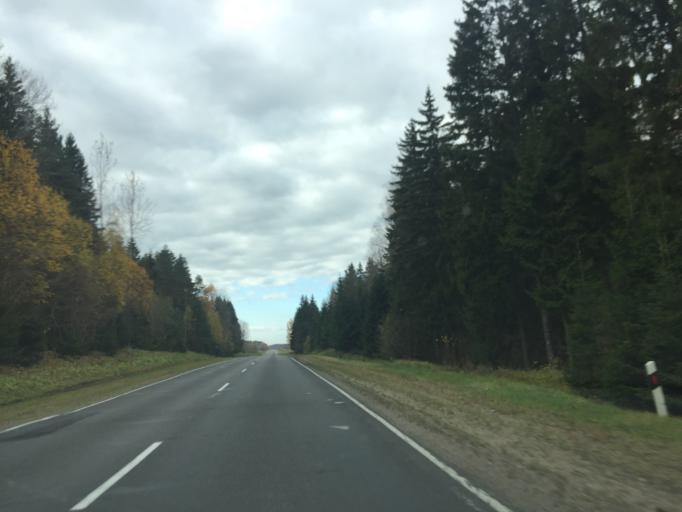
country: BY
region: Vitebsk
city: Mosar
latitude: 55.0663
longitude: 27.3213
